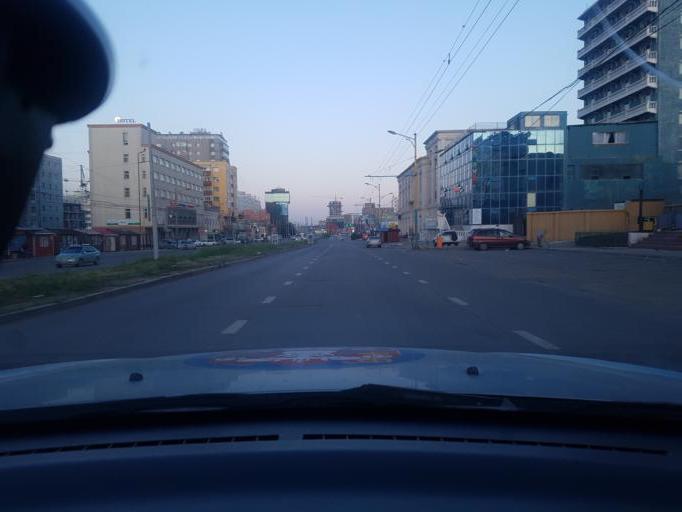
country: MN
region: Ulaanbaatar
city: Ulaanbaatar
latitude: 47.9226
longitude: 106.8693
